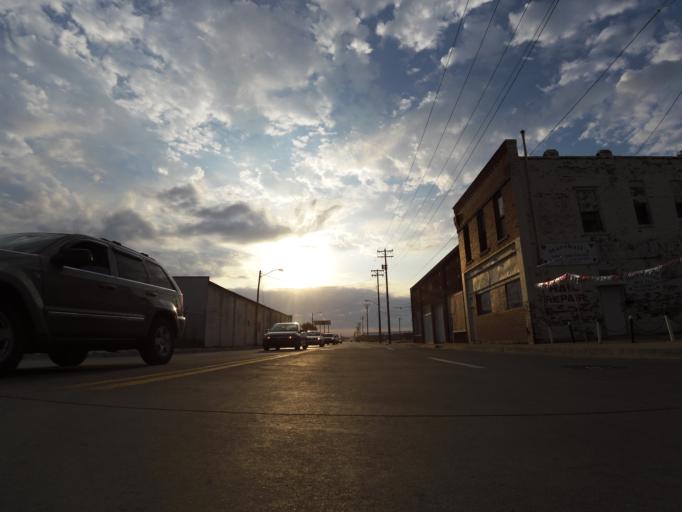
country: US
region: Kansas
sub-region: Sedgwick County
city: Wichita
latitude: 37.7226
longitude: -97.3345
